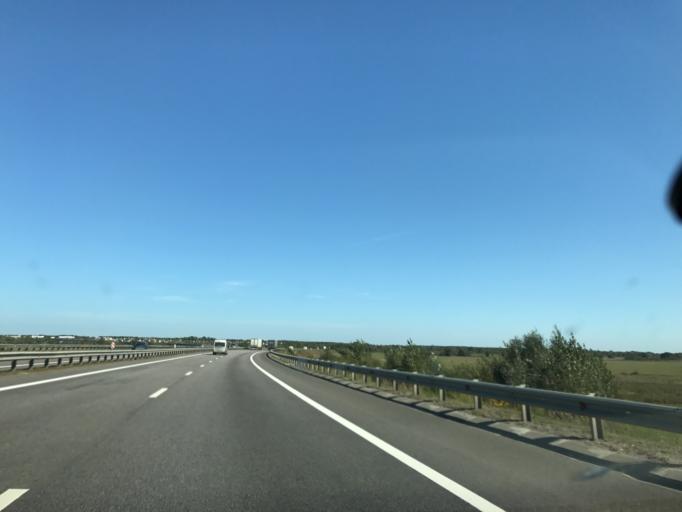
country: RU
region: Voronezj
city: Verkhniy Mamon
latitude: 50.1547
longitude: 40.4271
